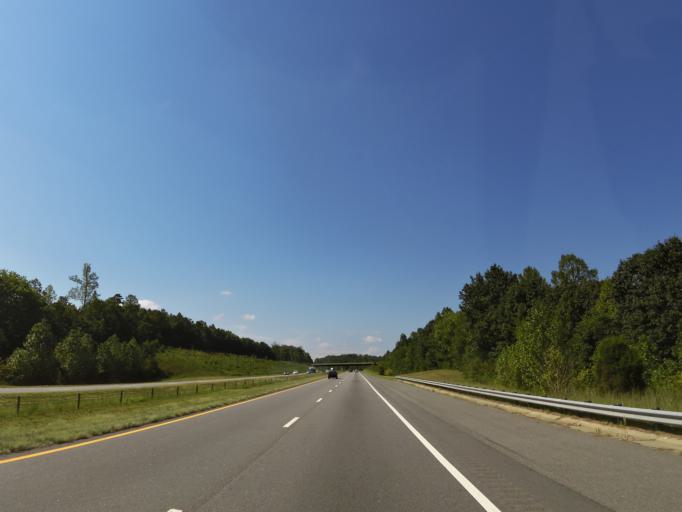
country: US
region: North Carolina
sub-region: Catawba County
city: Mountain View
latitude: 35.6533
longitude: -81.3149
